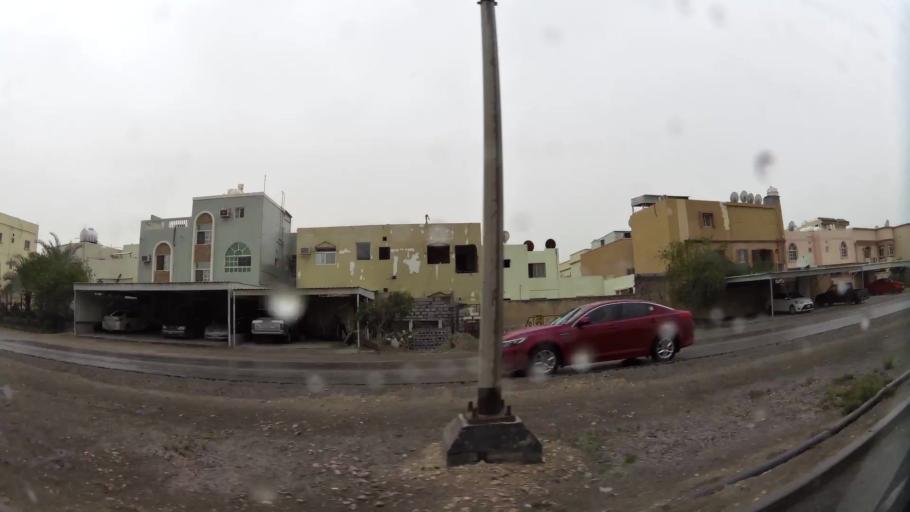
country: BH
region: Northern
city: Madinat `Isa
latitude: 26.1589
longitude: 50.5715
